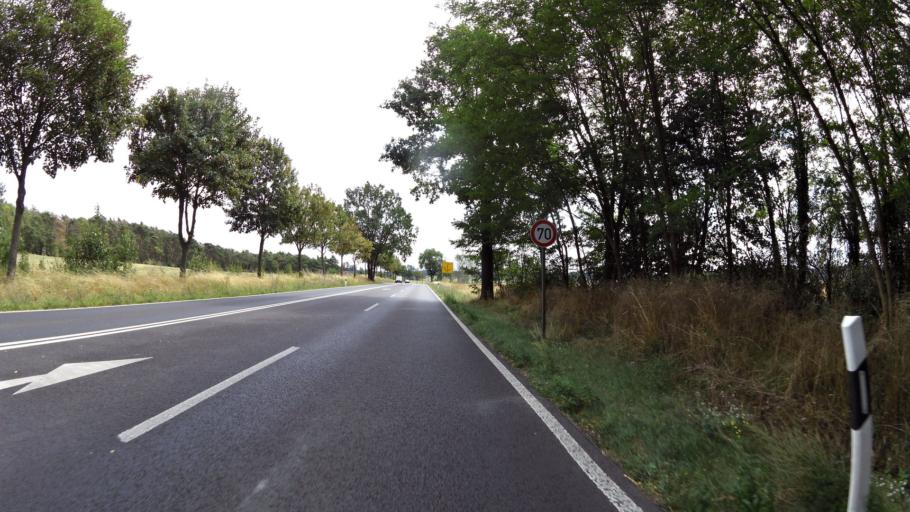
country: DE
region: Brandenburg
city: Neuzelle
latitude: 52.0803
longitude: 14.6592
